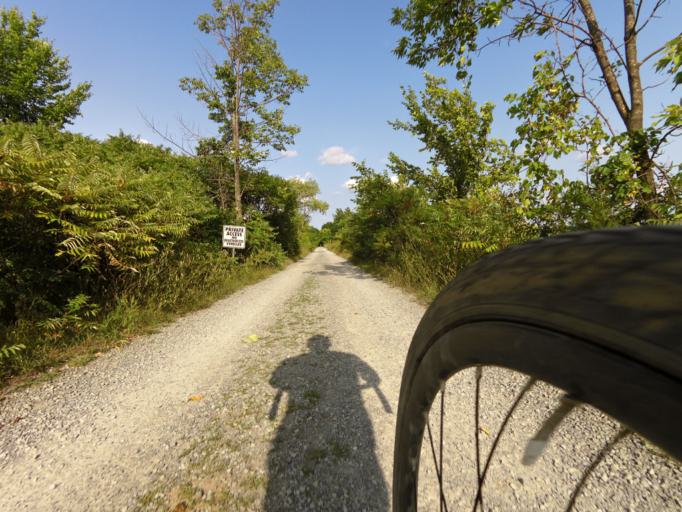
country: CA
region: Ontario
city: Kingston
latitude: 44.4269
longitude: -76.5617
